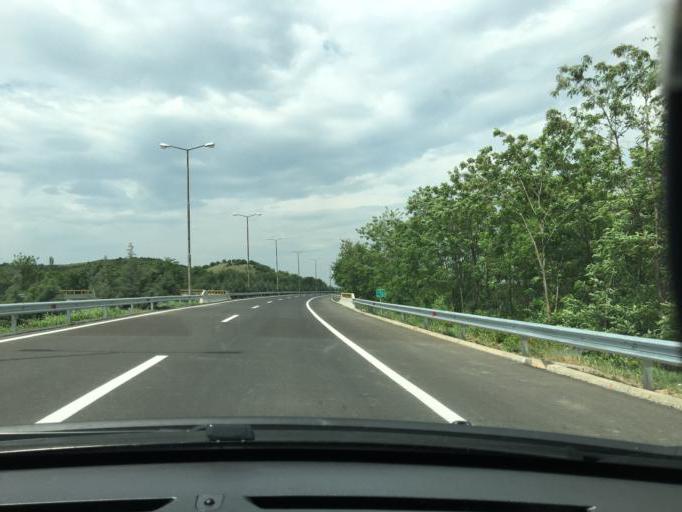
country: MK
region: Demir Kapija
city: Demir Kapija
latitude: 41.4166
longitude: 22.2313
